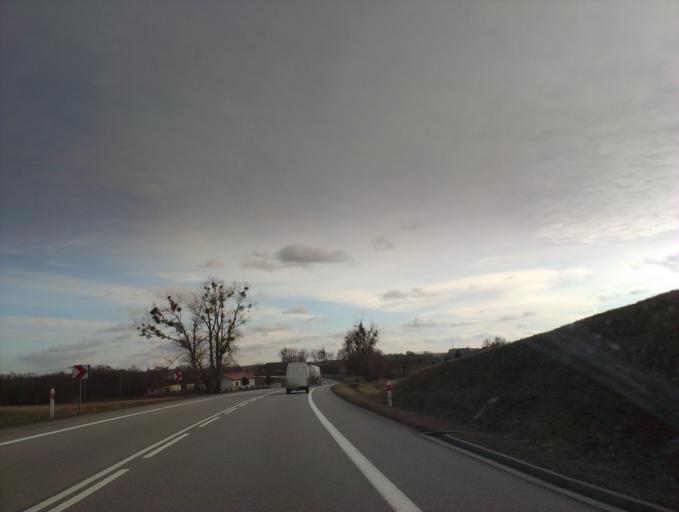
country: PL
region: Kujawsko-Pomorskie
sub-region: Powiat lipnowski
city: Kikol
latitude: 52.9217
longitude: 19.0951
